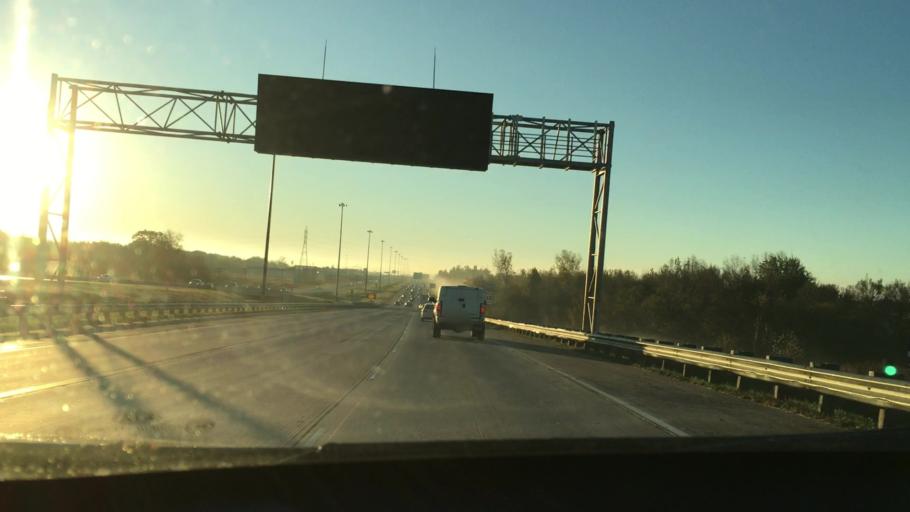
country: CA
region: Quebec
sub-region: Laurentides
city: Saint-Jerome
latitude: 45.7542
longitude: -74.0173
